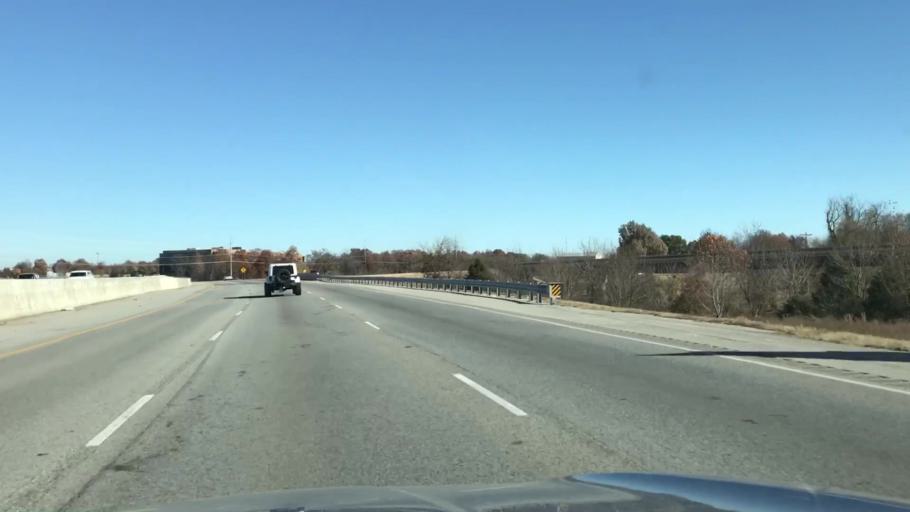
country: US
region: Arkansas
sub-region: Benton County
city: Lowell
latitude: 36.2396
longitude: -94.1561
